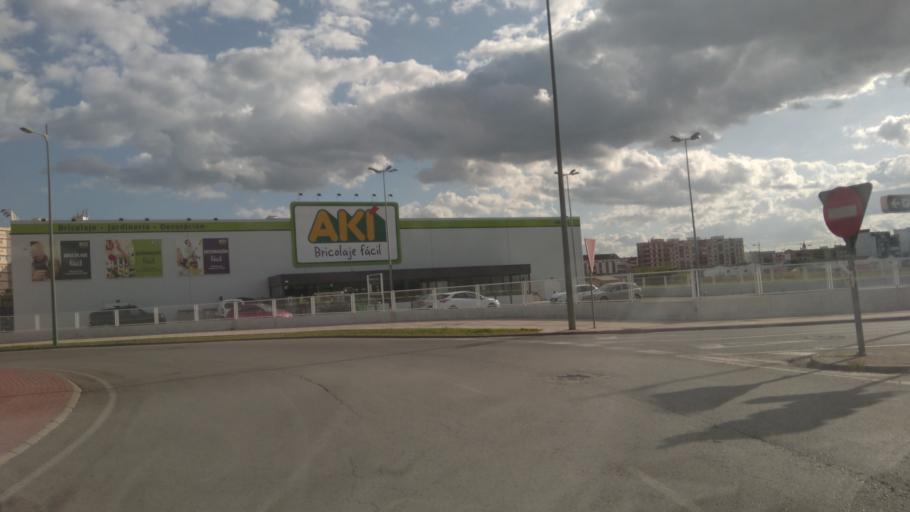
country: ES
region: Valencia
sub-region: Provincia de Valencia
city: Alzira
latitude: 39.1604
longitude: -0.4323
